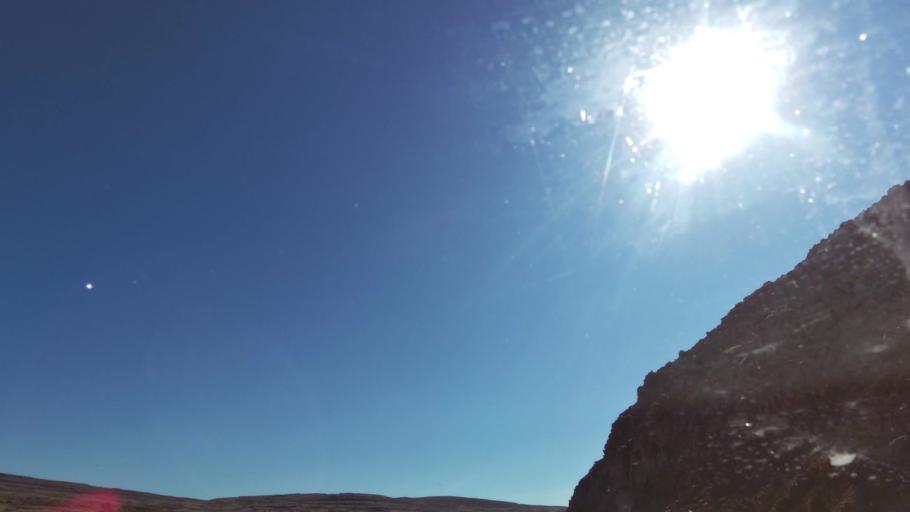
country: IS
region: West
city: Olafsvik
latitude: 65.5558
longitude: -24.1963
